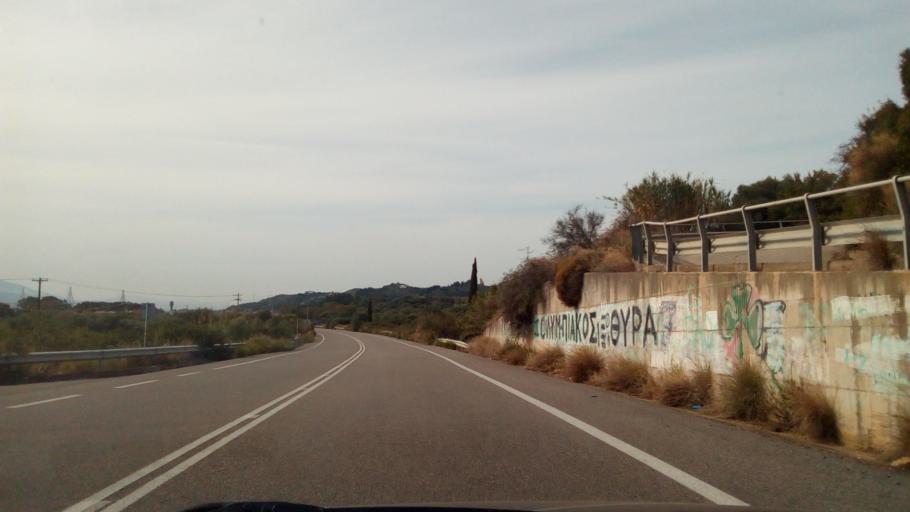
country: GR
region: West Greece
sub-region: Nomos Aitolias kai Akarnanias
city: Nafpaktos
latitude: 38.3752
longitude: 21.7831
